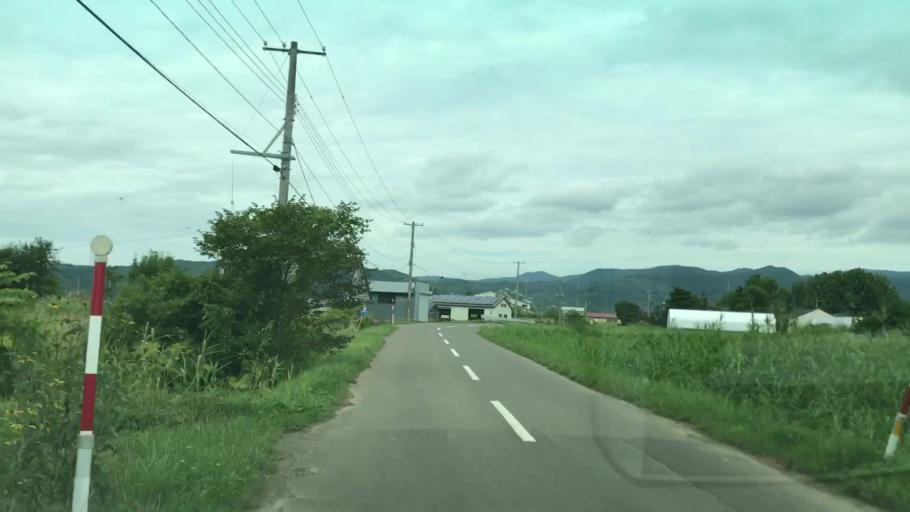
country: JP
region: Hokkaido
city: Iwanai
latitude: 43.0272
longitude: 140.5680
